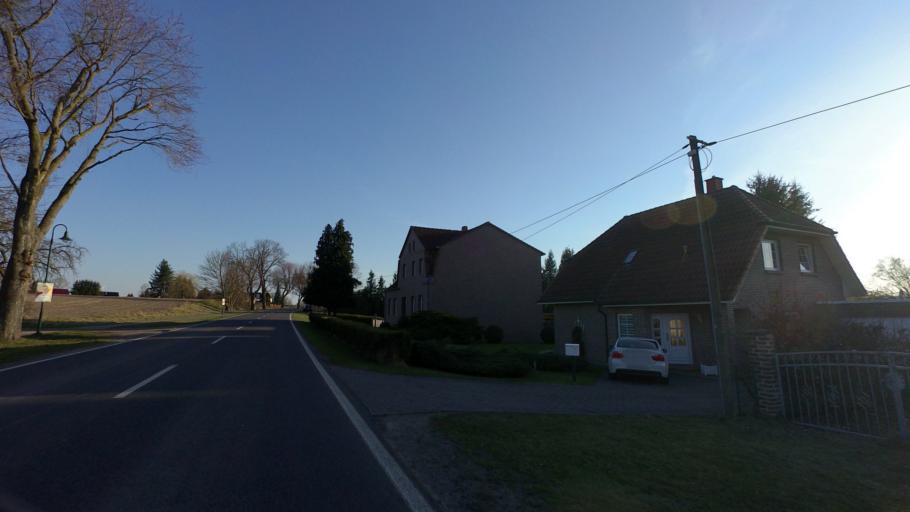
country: DE
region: Brandenburg
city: Eberswalde
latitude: 52.7841
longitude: 13.8392
